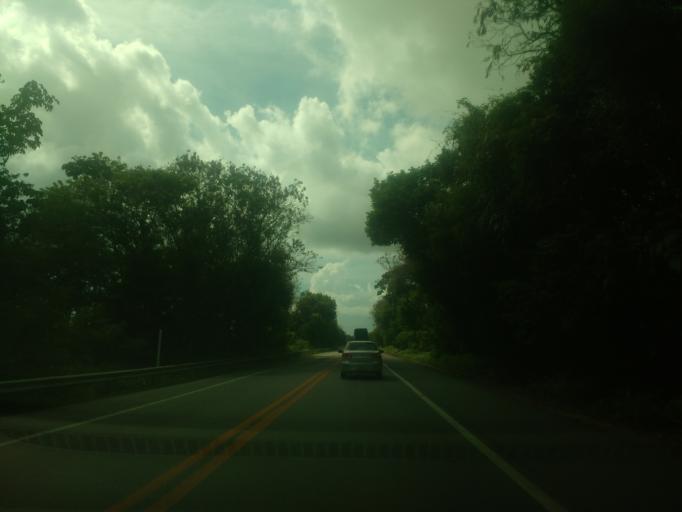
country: BR
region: Alagoas
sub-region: Marechal Deodoro
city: Marechal Deodoro
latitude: -9.6783
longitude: -35.8333
